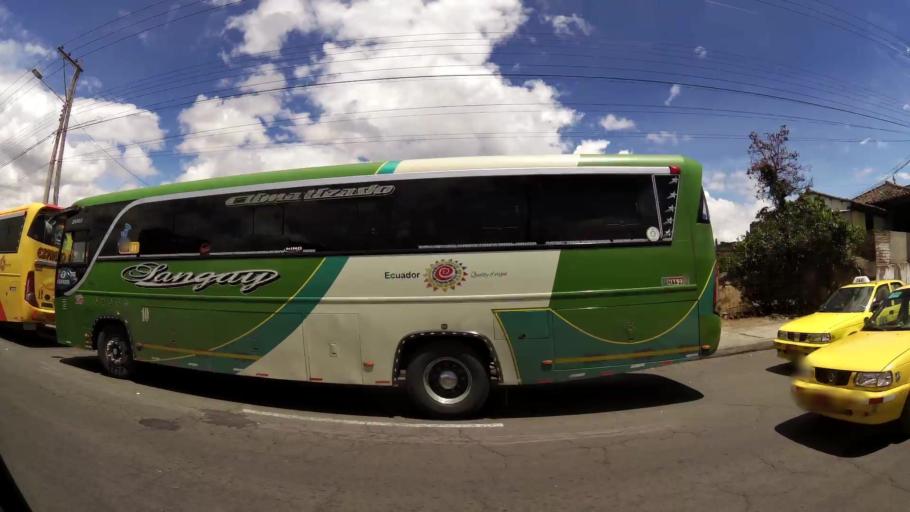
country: EC
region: Tungurahua
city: Ambato
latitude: -1.2743
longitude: -78.6110
